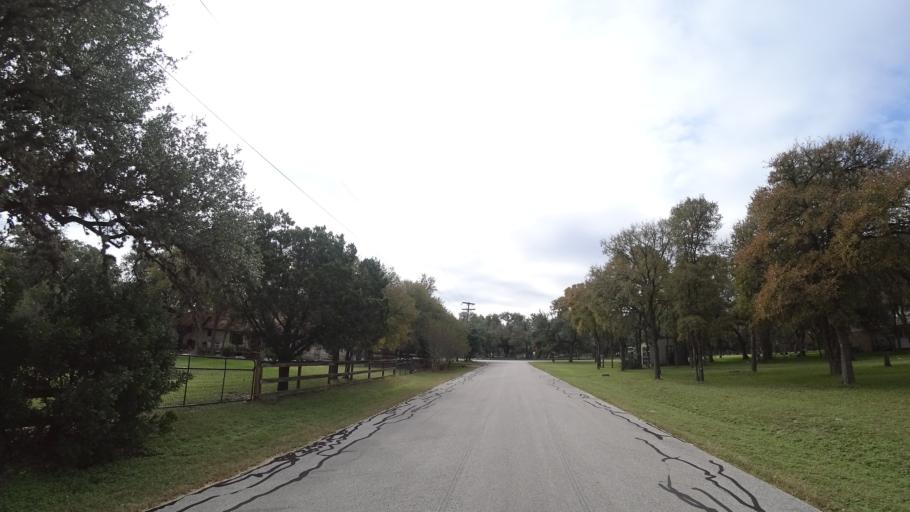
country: US
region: Texas
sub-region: Travis County
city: Shady Hollow
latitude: 30.1367
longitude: -97.8857
